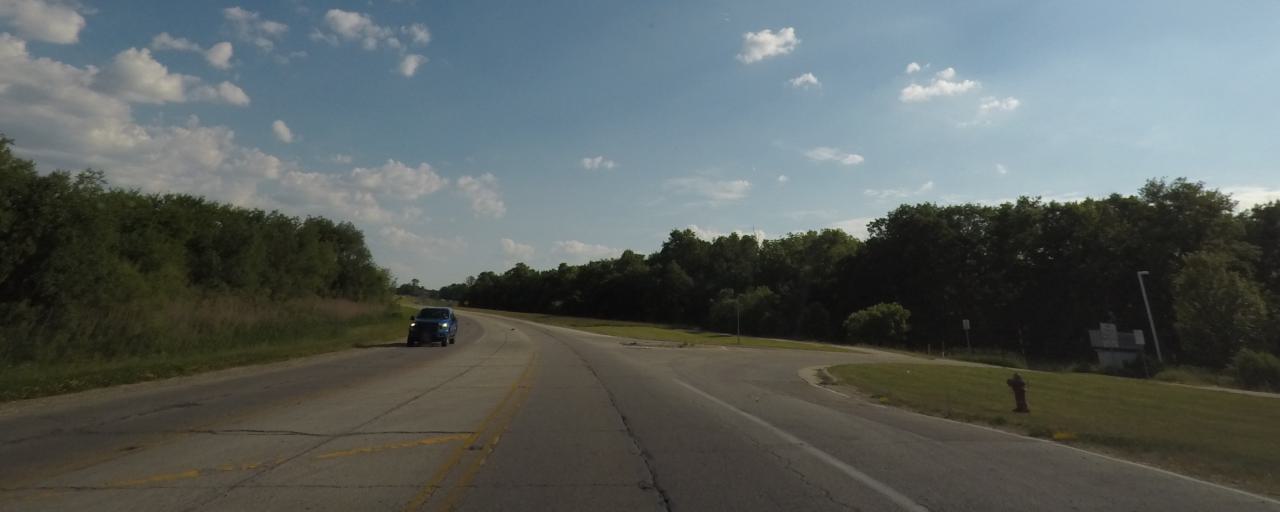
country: US
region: Wisconsin
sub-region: Waukesha County
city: New Berlin
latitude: 42.9372
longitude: -88.1130
